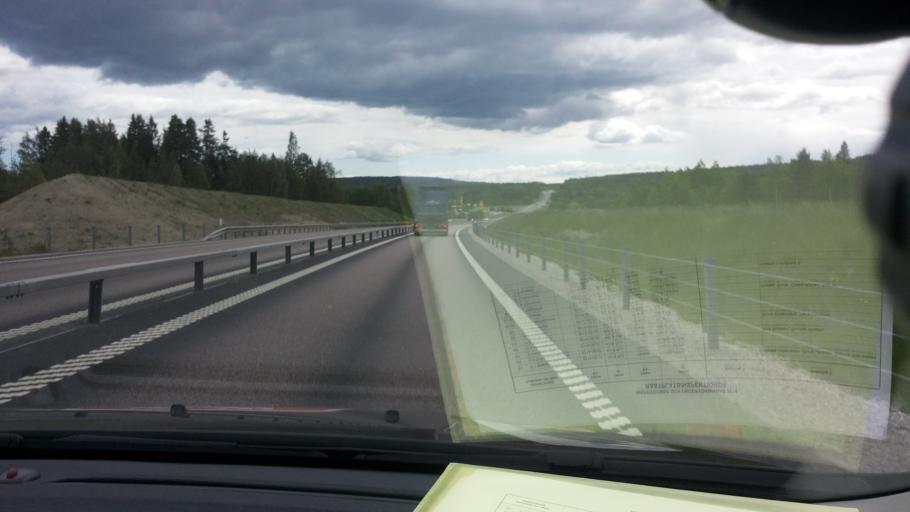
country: SE
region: Vaesternorrland
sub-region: Sundsvalls Kommun
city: Njurundabommen
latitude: 62.2551
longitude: 17.3698
